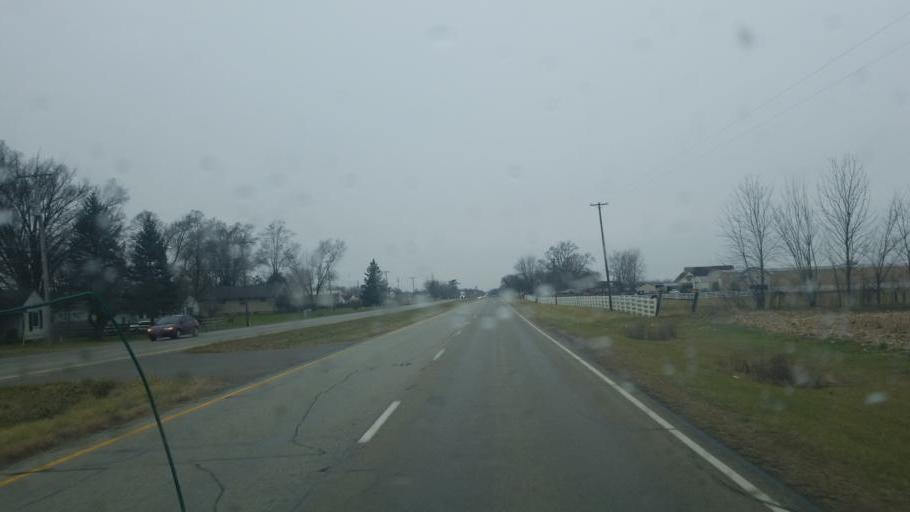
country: US
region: Indiana
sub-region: Hancock County
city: Greenfield
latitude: 39.7874
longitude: -85.7230
